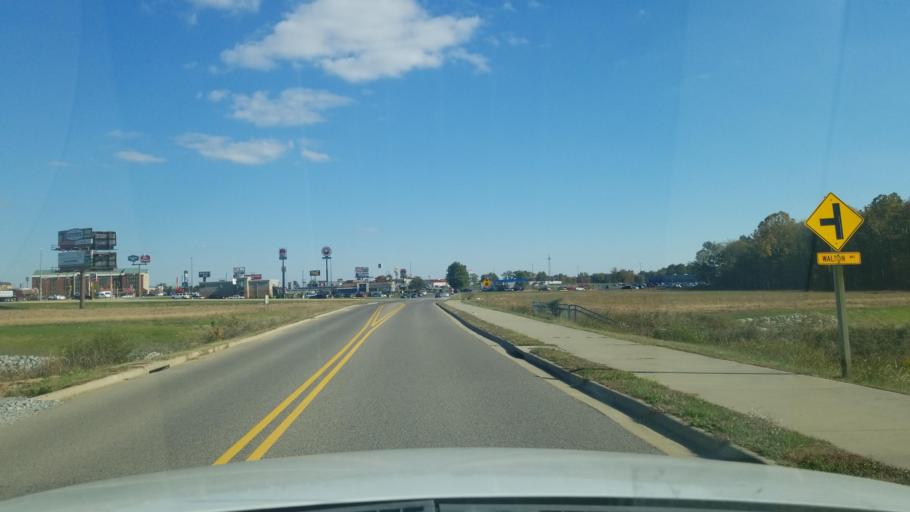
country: US
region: Illinois
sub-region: Williamson County
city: Marion
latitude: 37.7427
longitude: -88.9729
